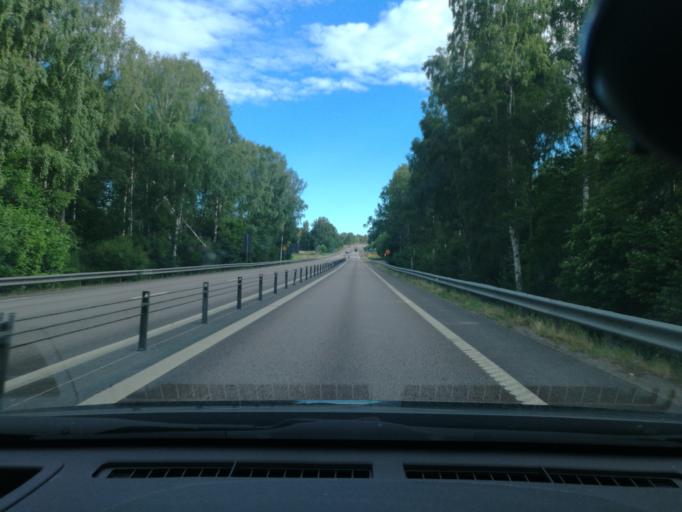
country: SE
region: Kalmar
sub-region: Oskarshamns Kommun
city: Oskarshamn
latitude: 57.4150
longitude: 16.4817
